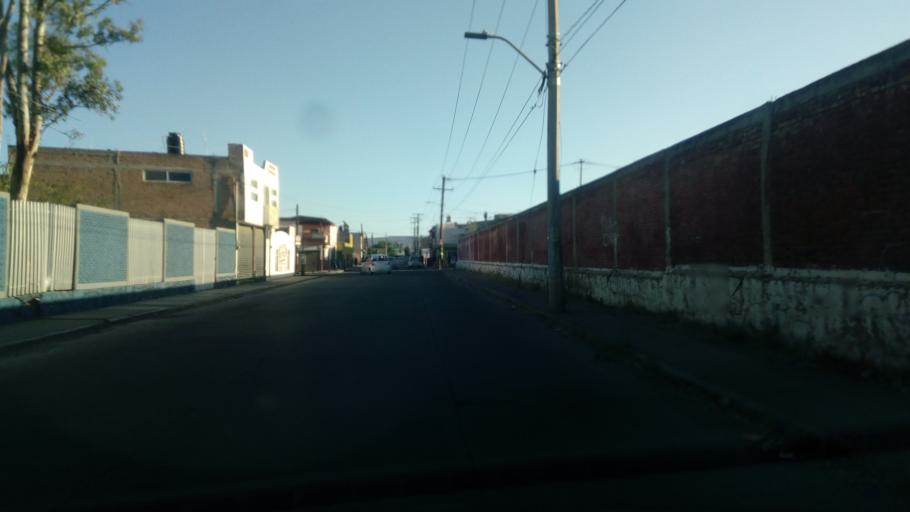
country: MX
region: Durango
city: Victoria de Durango
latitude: 24.0030
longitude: -104.6793
